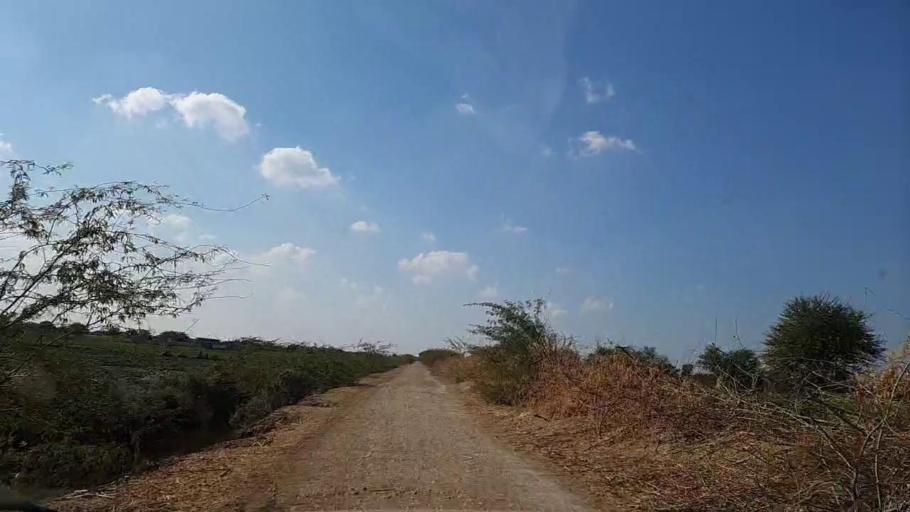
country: PK
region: Sindh
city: Pithoro
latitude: 25.6141
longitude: 69.4114
